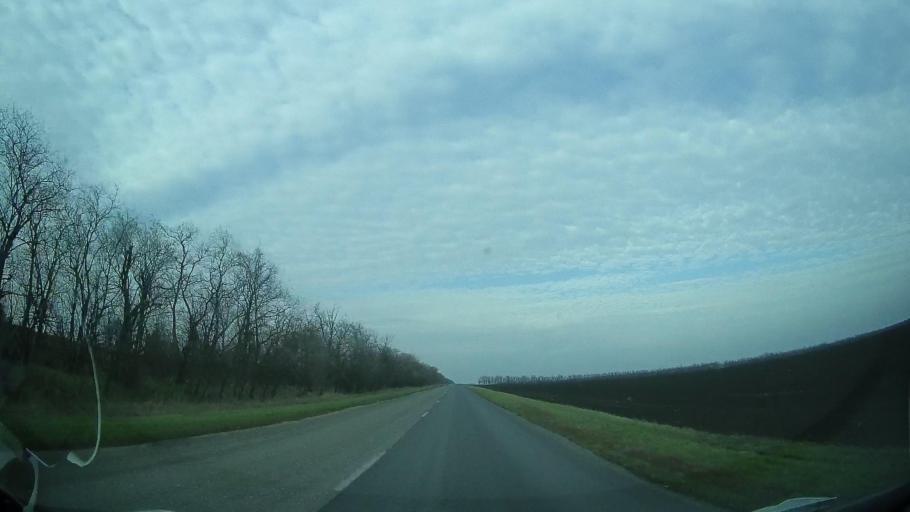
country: RU
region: Rostov
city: Zernograd
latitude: 46.9337
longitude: 40.3665
